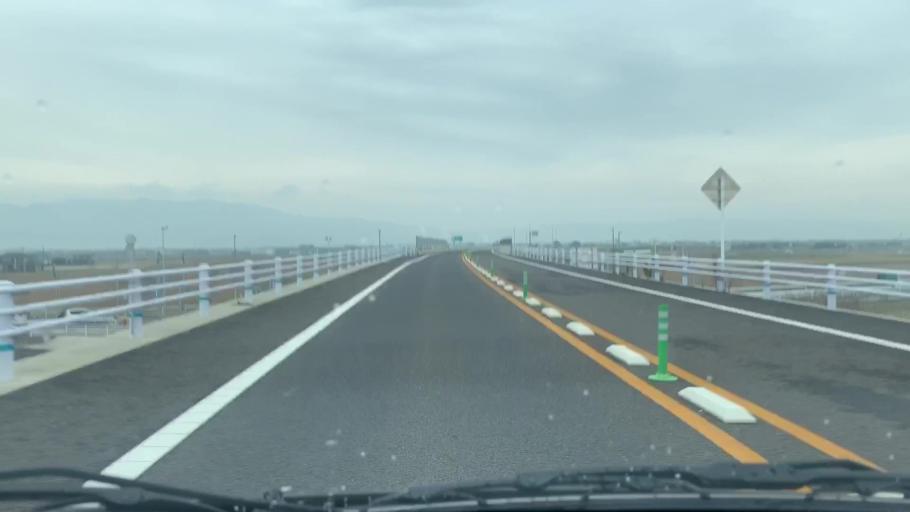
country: JP
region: Saga Prefecture
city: Saga-shi
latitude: 33.2198
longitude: 130.2145
